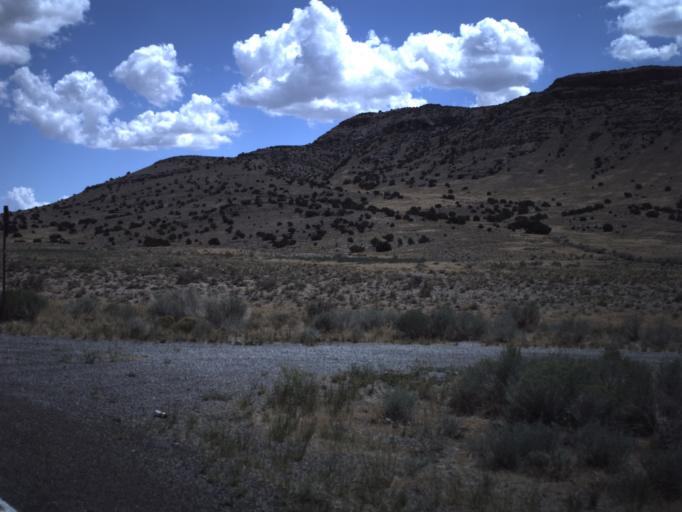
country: US
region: Utah
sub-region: Beaver County
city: Milford
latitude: 39.0721
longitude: -113.6479
